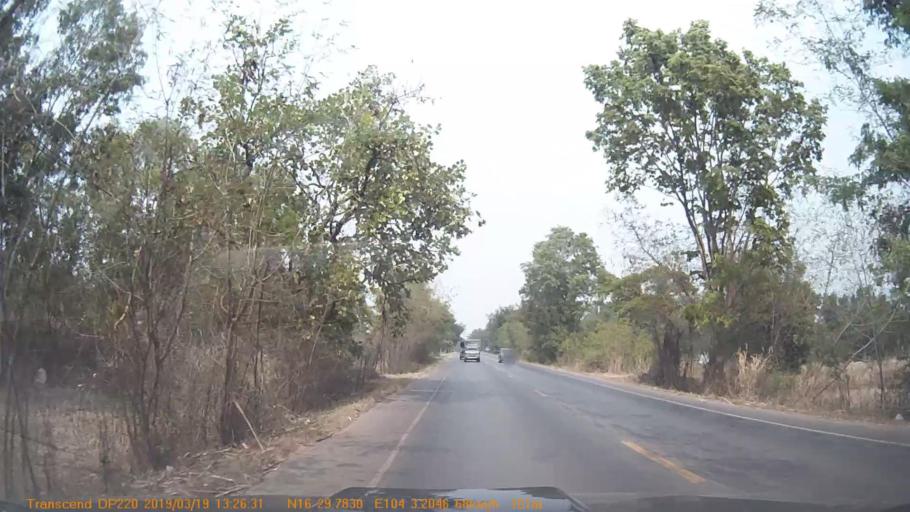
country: TH
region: Kalasin
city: Kuchinarai
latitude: 16.4965
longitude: 104.0535
